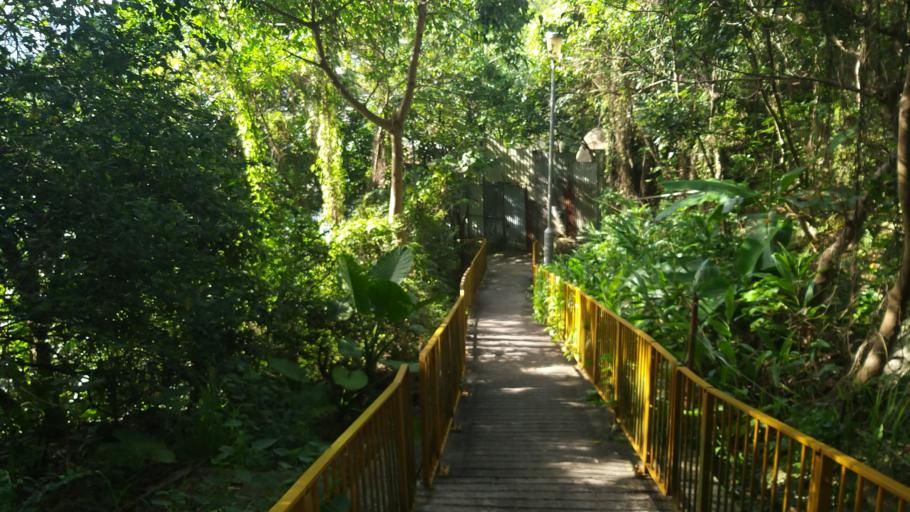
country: HK
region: Tuen Mun
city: Tuen Mun
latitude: 22.3945
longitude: 113.9806
